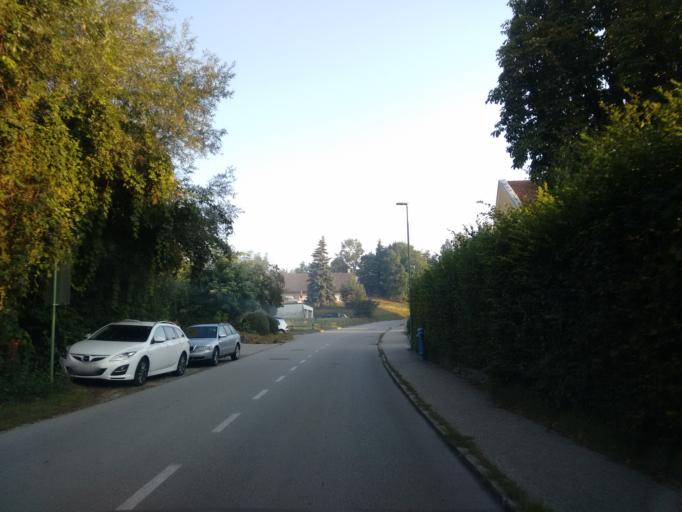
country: AT
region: Upper Austria
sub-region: Wels Stadt
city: Wels
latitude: 48.1850
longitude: 14.0033
